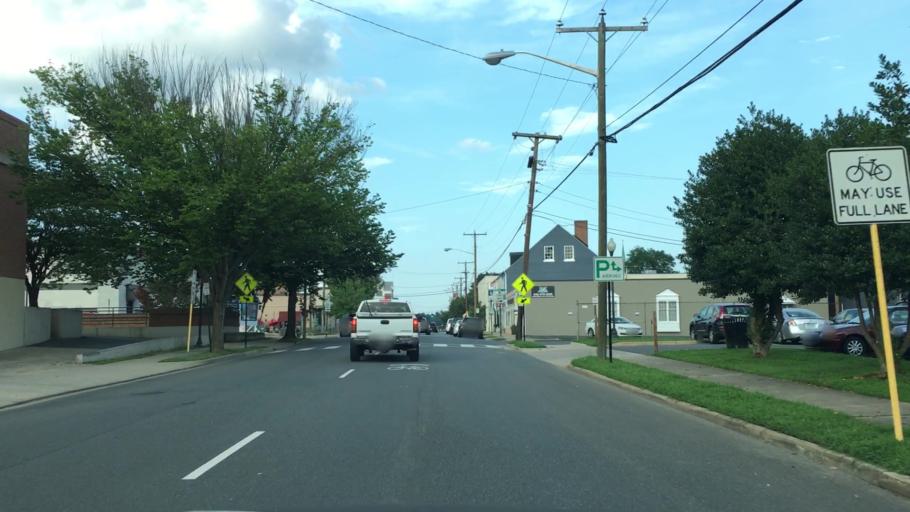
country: US
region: Virginia
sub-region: City of Fredericksburg
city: Fredericksburg
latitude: 38.3014
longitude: -77.4652
